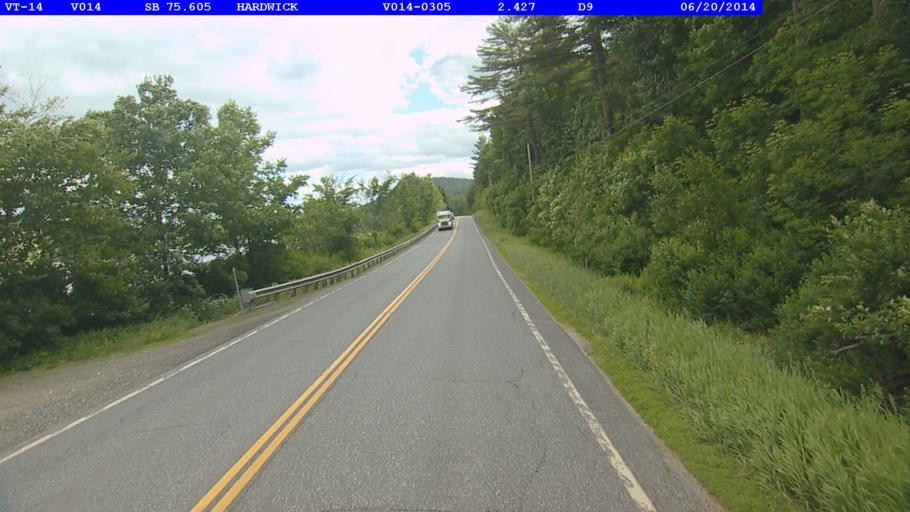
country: US
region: Vermont
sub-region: Caledonia County
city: Hardwick
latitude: 44.5291
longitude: -72.3742
